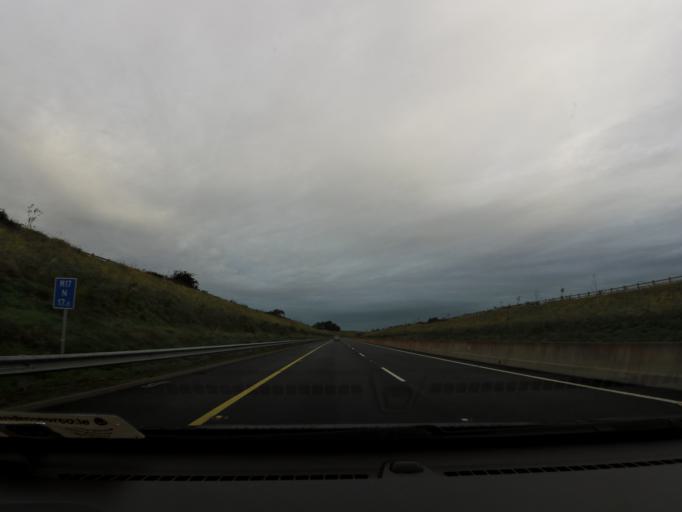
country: IE
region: Connaught
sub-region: County Galway
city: Tuam
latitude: 53.4413
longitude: -8.8483
